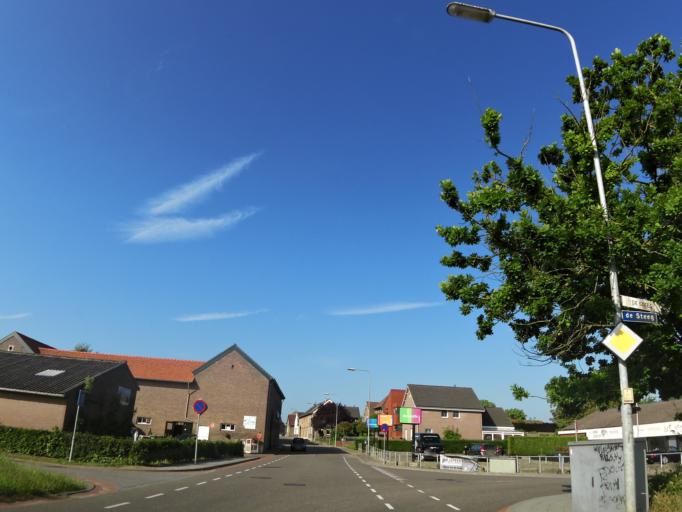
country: NL
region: Limburg
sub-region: Valkenburg aan de Geul
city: Broekhem
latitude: 50.8933
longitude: 5.8225
